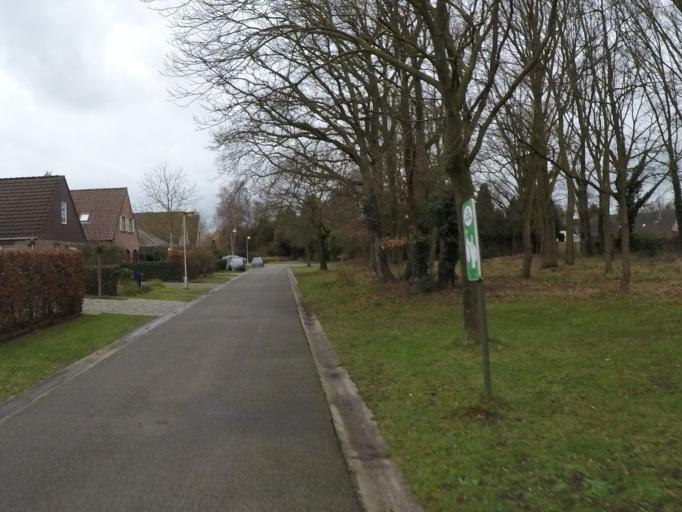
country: BE
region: Flanders
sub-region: Provincie Antwerpen
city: Schilde
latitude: 51.2156
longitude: 4.5894
